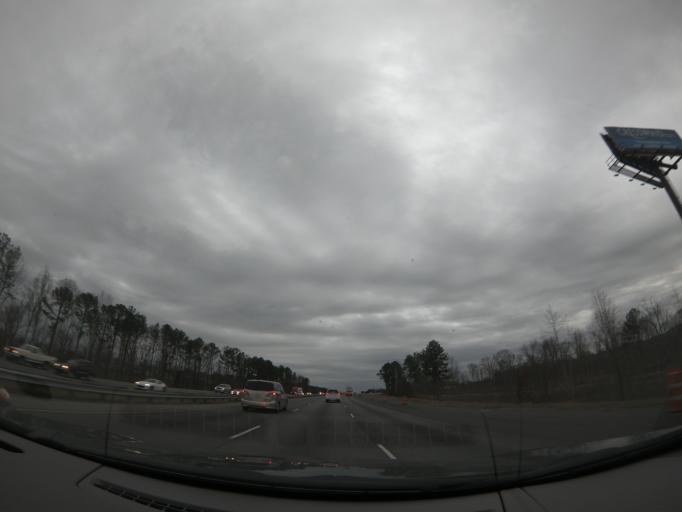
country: US
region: Georgia
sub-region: Whitfield County
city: Dalton
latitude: 34.6590
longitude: -84.9862
